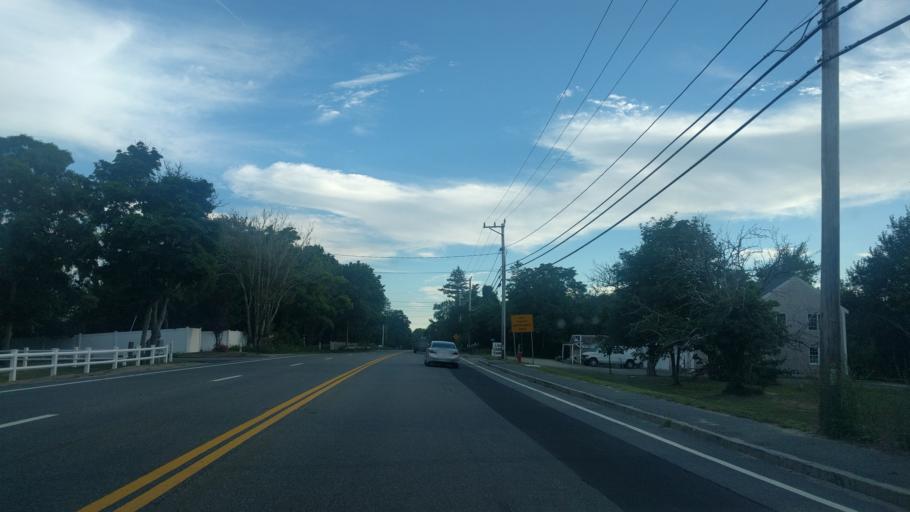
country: US
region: Massachusetts
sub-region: Barnstable County
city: Orleans
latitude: 41.8040
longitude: -69.9772
